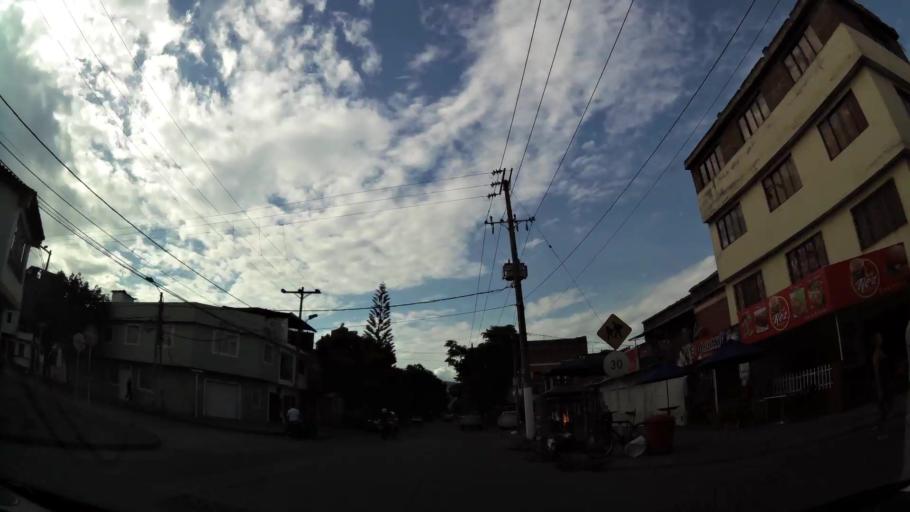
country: CO
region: Valle del Cauca
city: Cali
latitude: 3.4629
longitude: -76.5060
